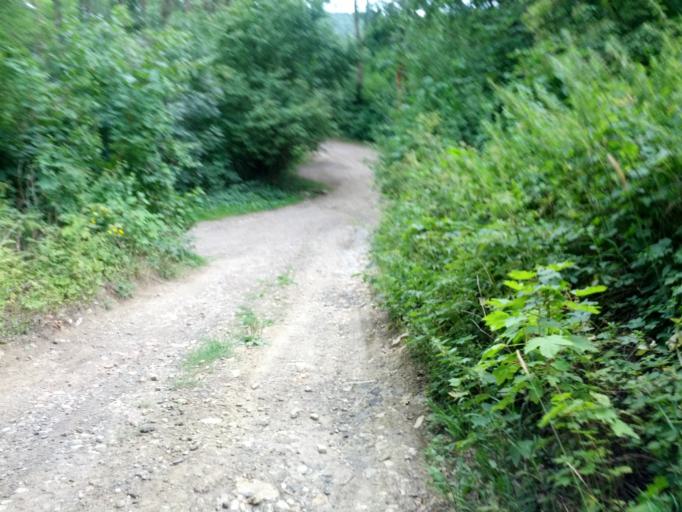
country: DE
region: Thuringia
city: Eisenach
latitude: 50.9840
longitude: 10.3476
